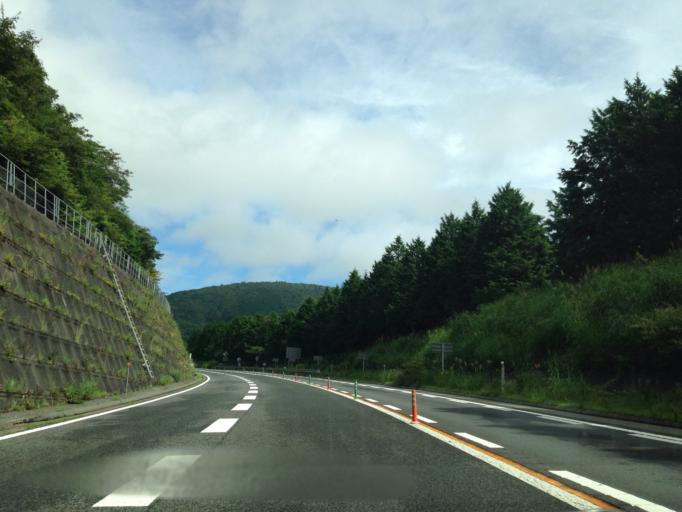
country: JP
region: Shizuoka
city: Gotemba
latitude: 35.3716
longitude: 138.8496
